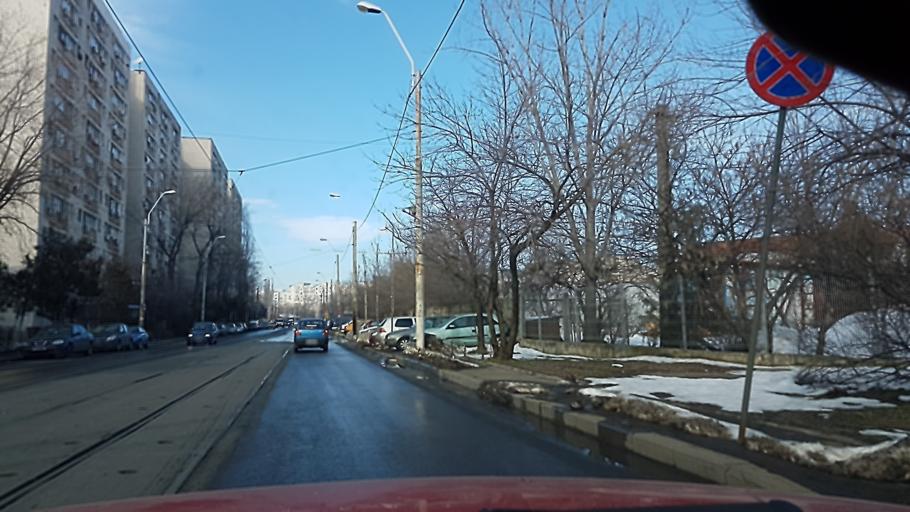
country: RO
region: Ilfov
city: Dobroesti
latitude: 44.4308
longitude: 26.1733
